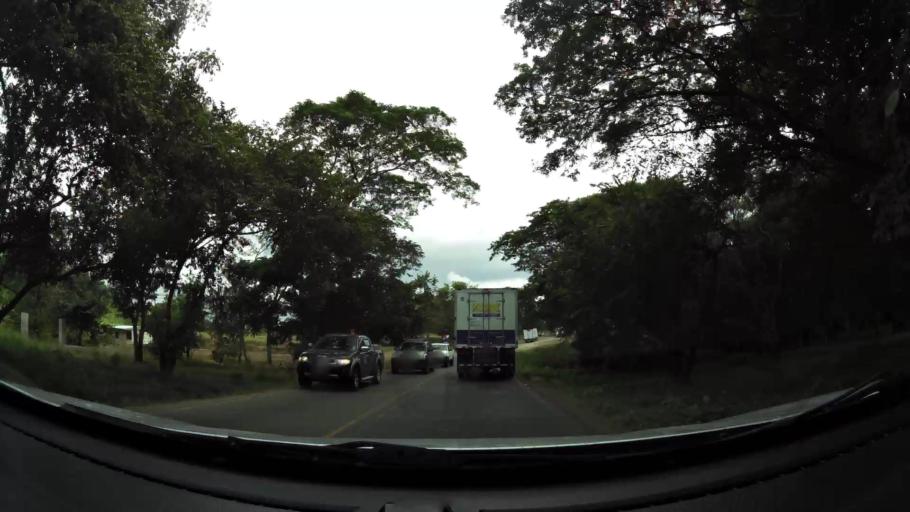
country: CR
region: Guanacaste
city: Juntas
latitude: 10.1714
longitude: -84.9228
